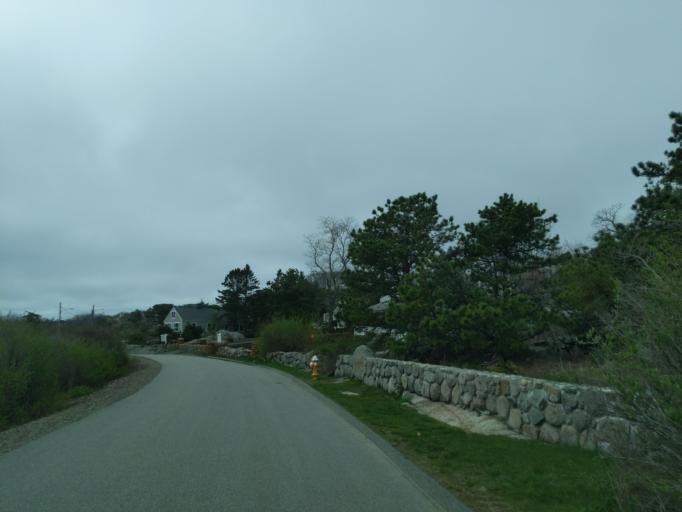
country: US
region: Massachusetts
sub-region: Essex County
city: Rockport
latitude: 42.6441
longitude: -70.5957
